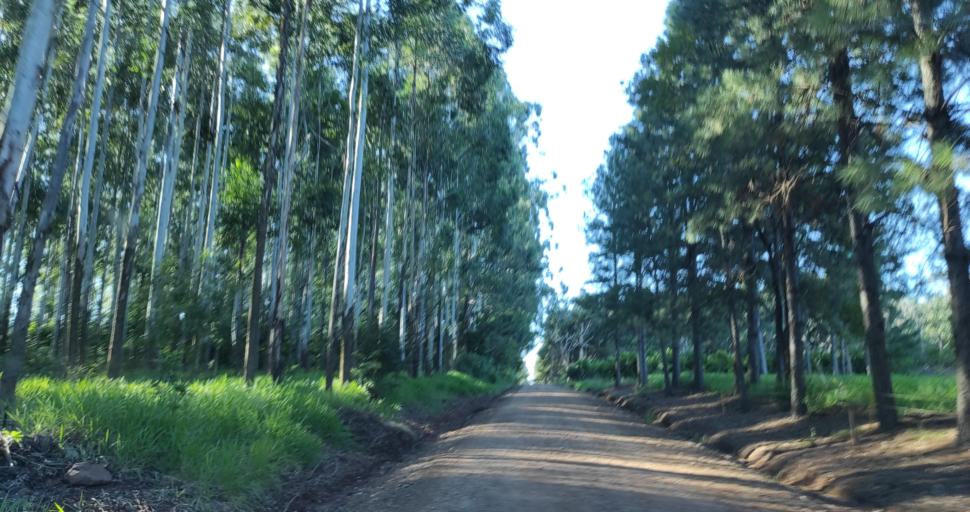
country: AR
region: Misiones
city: Garuhape
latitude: -26.8605
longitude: -55.0044
